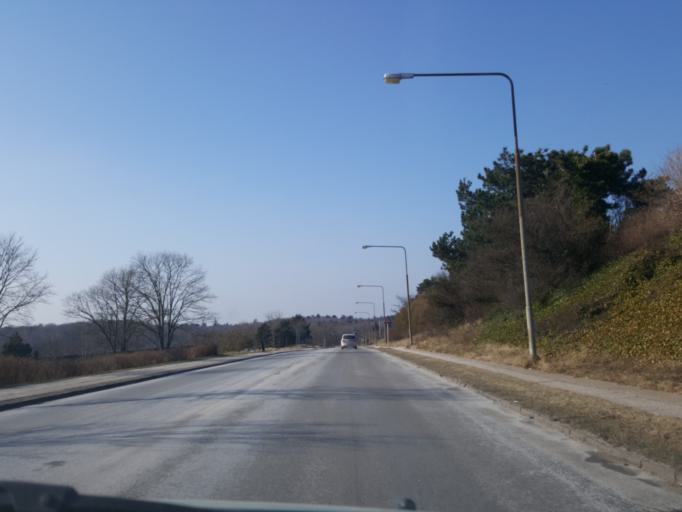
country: DK
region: Zealand
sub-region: Kalundborg Kommune
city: Kalundborg
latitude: 55.6858
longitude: 11.0822
